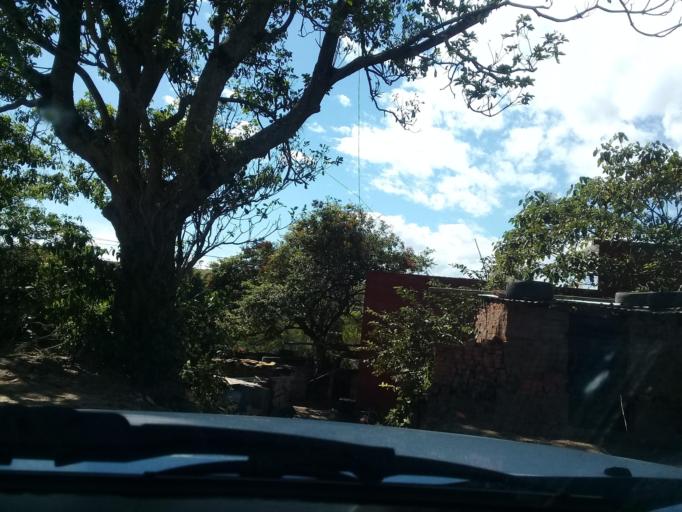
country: MX
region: Veracruz
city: El Castillo
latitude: 19.5502
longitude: -96.8539
